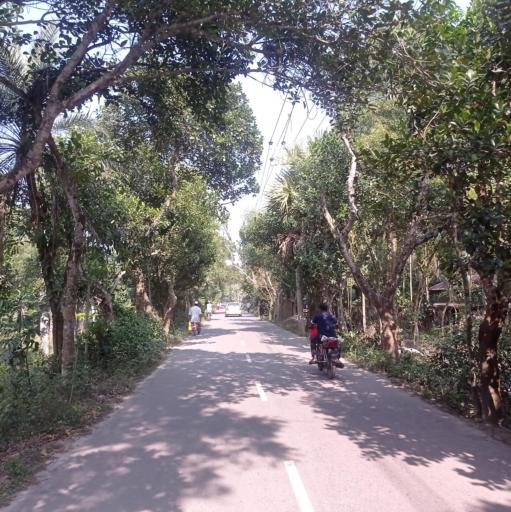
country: BD
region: Dhaka
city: Narsingdi
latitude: 24.0716
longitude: 90.6927
